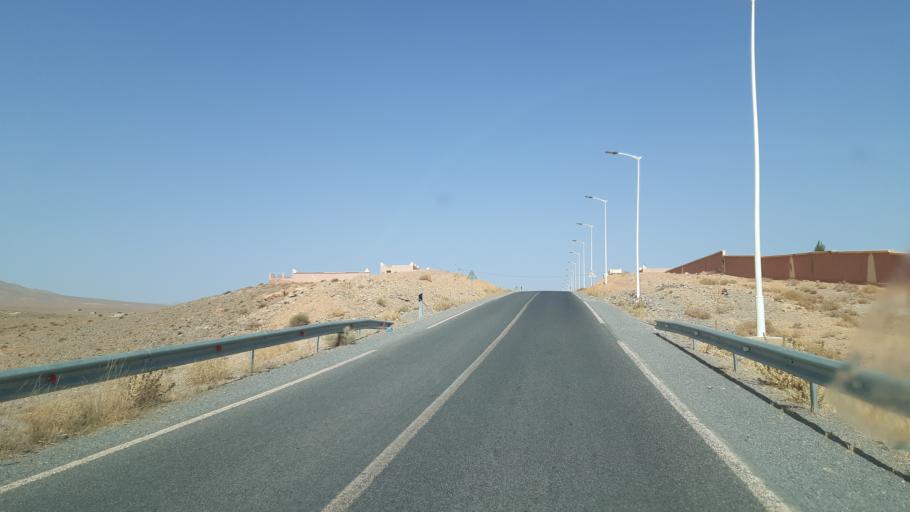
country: MA
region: Meknes-Tafilalet
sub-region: Errachidia
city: Amouguer
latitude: 32.2221
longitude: -4.6773
